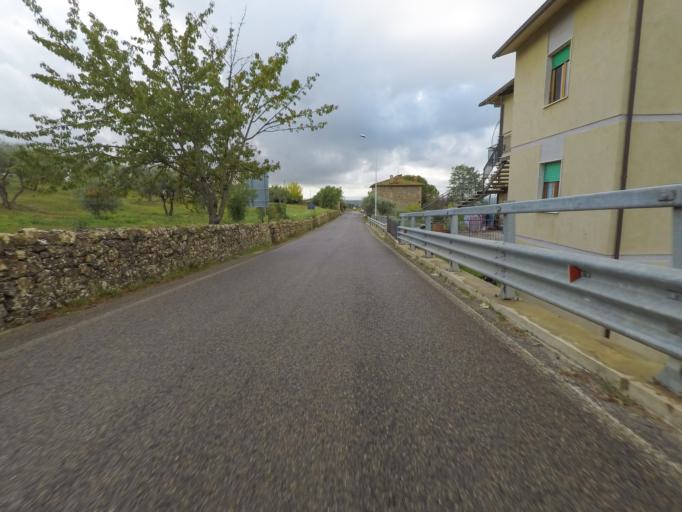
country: IT
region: Tuscany
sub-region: Provincia di Siena
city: Belverde
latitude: 43.3943
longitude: 11.3470
